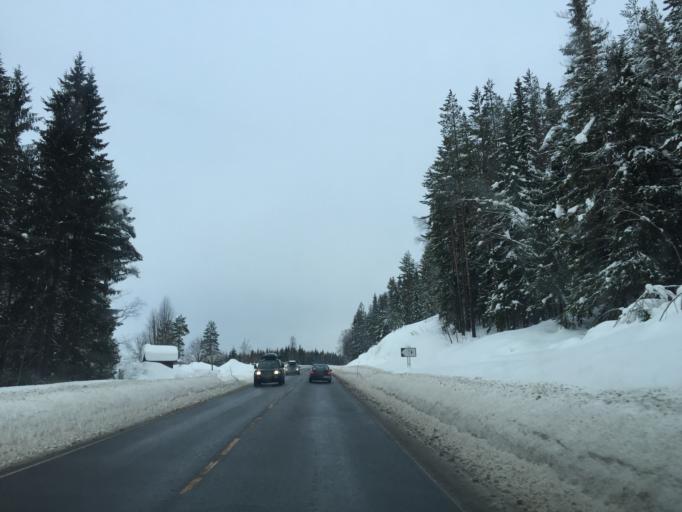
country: NO
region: Hedmark
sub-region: Trysil
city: Innbygda
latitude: 61.0937
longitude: 12.0023
